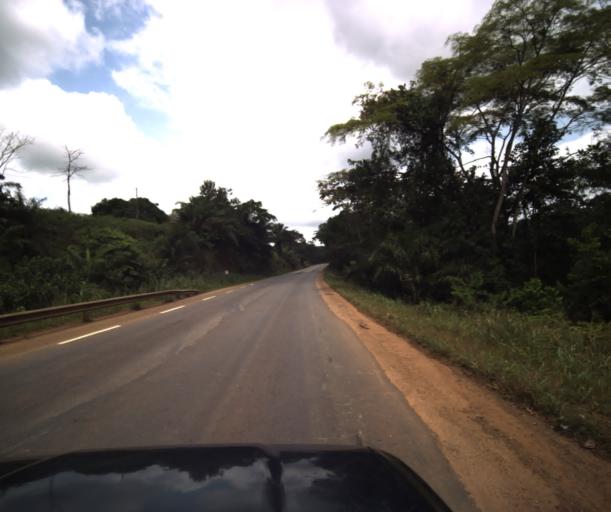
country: CM
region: Centre
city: Mbankomo
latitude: 3.7775
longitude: 11.0764
